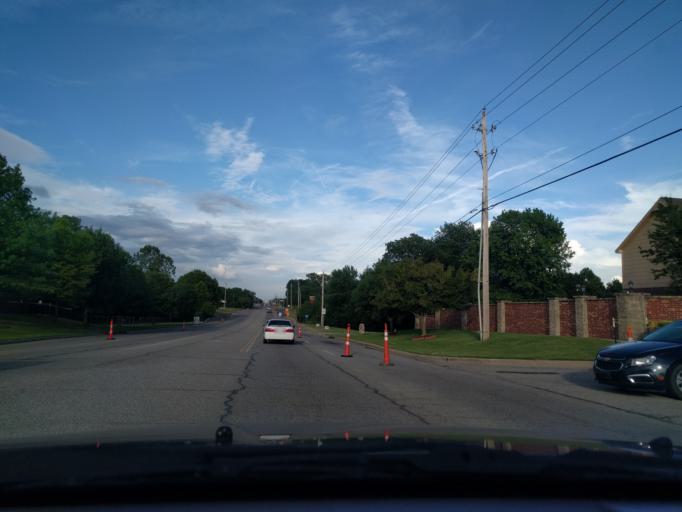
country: US
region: Oklahoma
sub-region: Tulsa County
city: Broken Arrow
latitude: 36.0609
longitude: -95.8405
